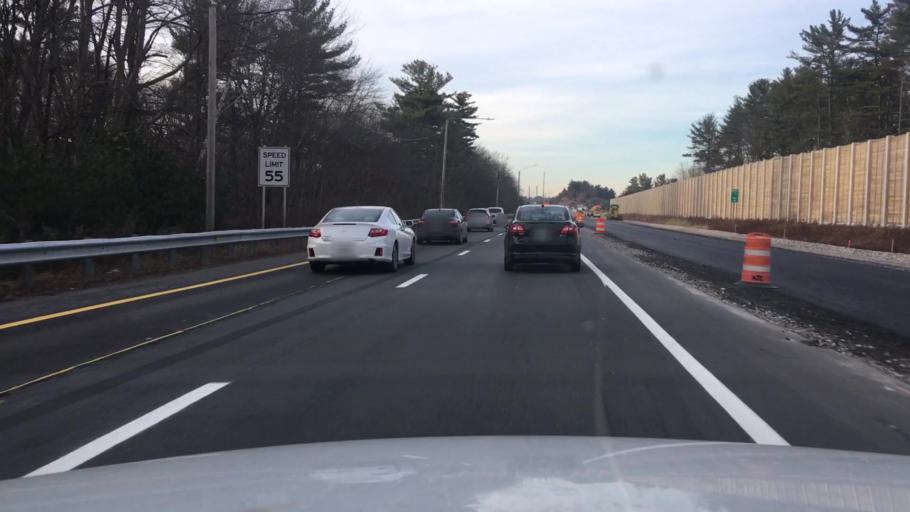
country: US
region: New Hampshire
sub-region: Rockingham County
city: Auburn
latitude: 42.9498
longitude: -71.3970
